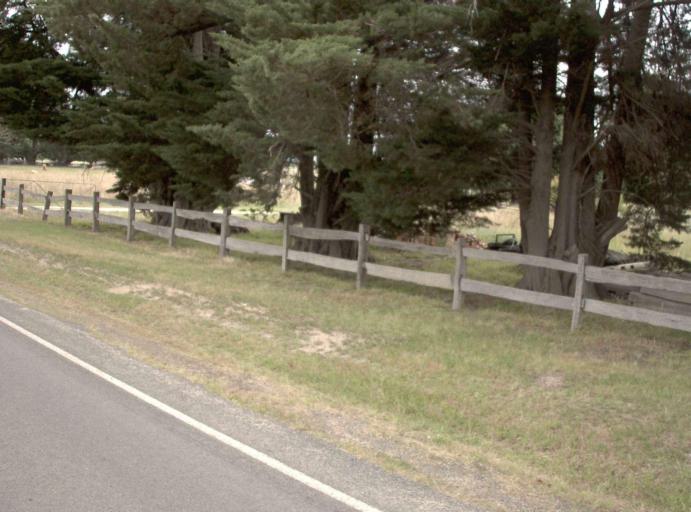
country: AU
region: Victoria
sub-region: Latrobe
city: Traralgon
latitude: -38.5198
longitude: 146.6610
